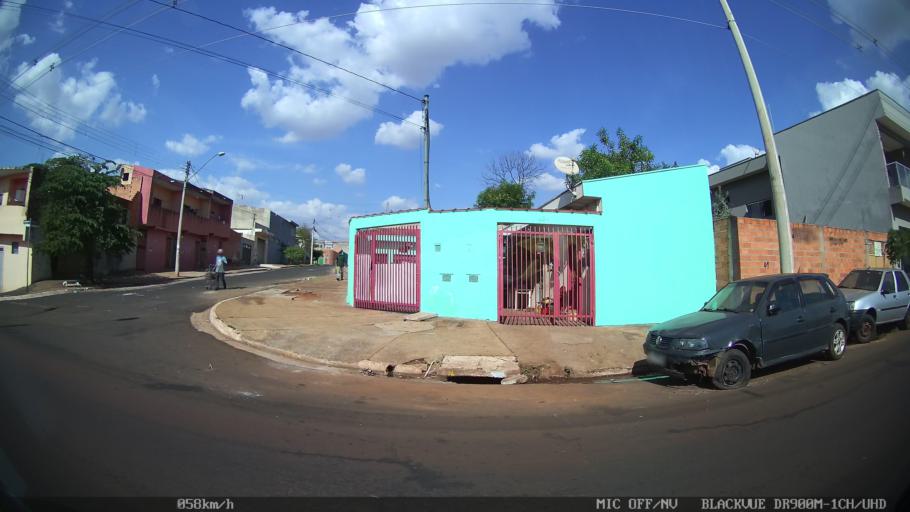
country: BR
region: Sao Paulo
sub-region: Ribeirao Preto
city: Ribeirao Preto
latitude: -21.1974
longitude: -47.8527
